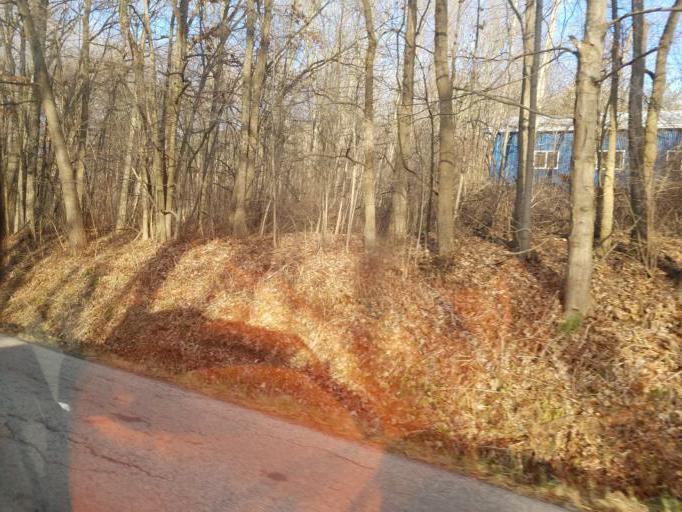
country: US
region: Ohio
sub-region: Sandusky County
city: Bellville
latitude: 40.6077
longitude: -82.3780
